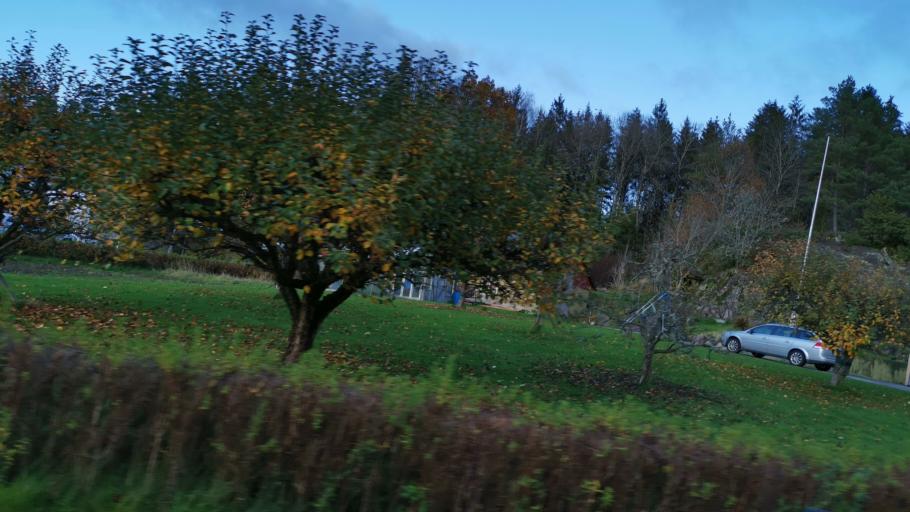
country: SE
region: Vaestra Goetaland
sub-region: Munkedals Kommun
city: Munkedal
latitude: 58.4773
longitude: 11.6697
